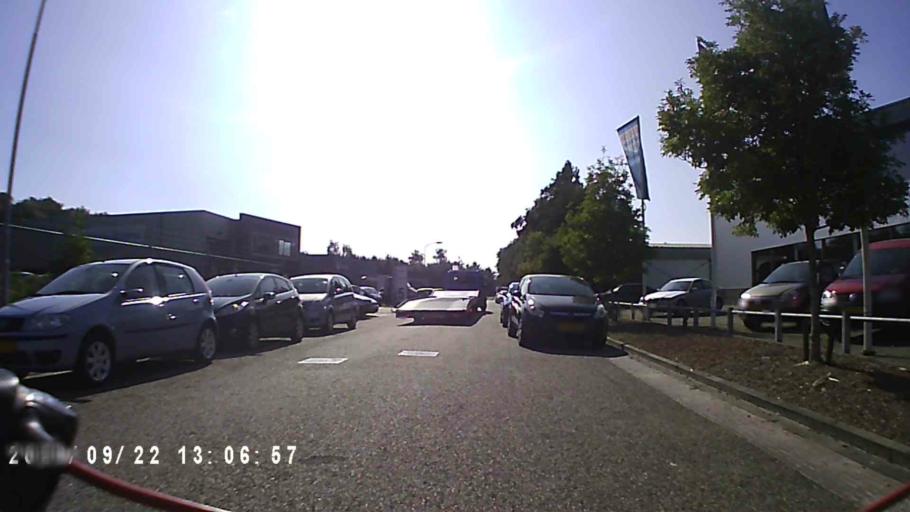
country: NL
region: Groningen
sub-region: Gemeente Leek
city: Leek
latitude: 53.1798
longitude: 6.3759
